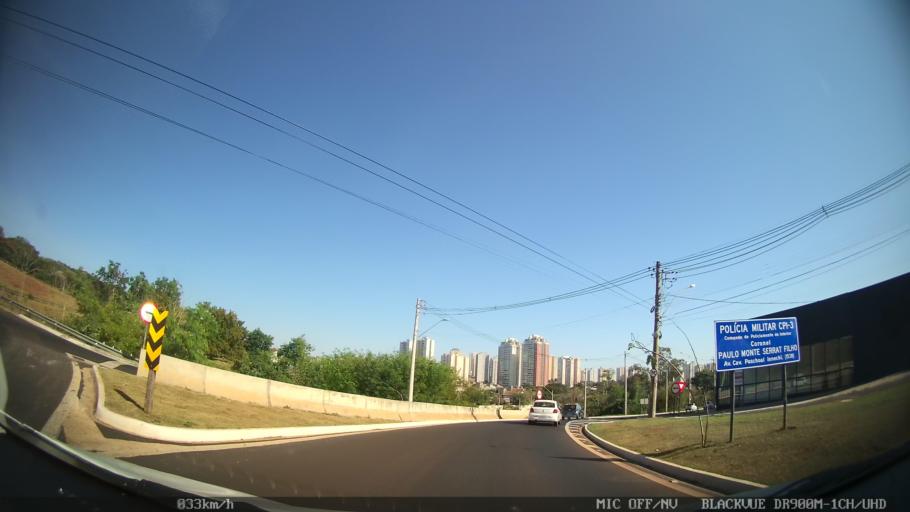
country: BR
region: Sao Paulo
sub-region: Ribeirao Preto
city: Ribeirao Preto
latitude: -21.2208
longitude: -47.7890
